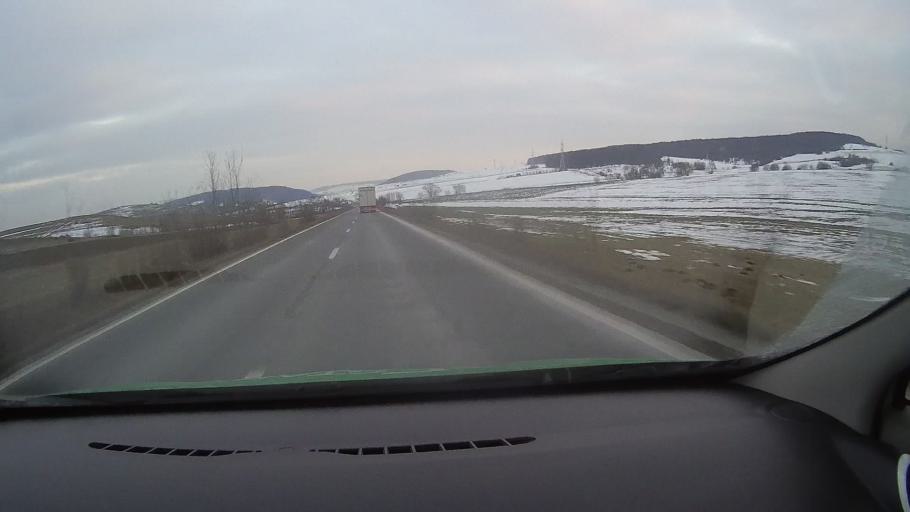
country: RO
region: Harghita
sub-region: Comuna Lupeni
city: Lupeni
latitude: 46.3561
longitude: 25.2522
